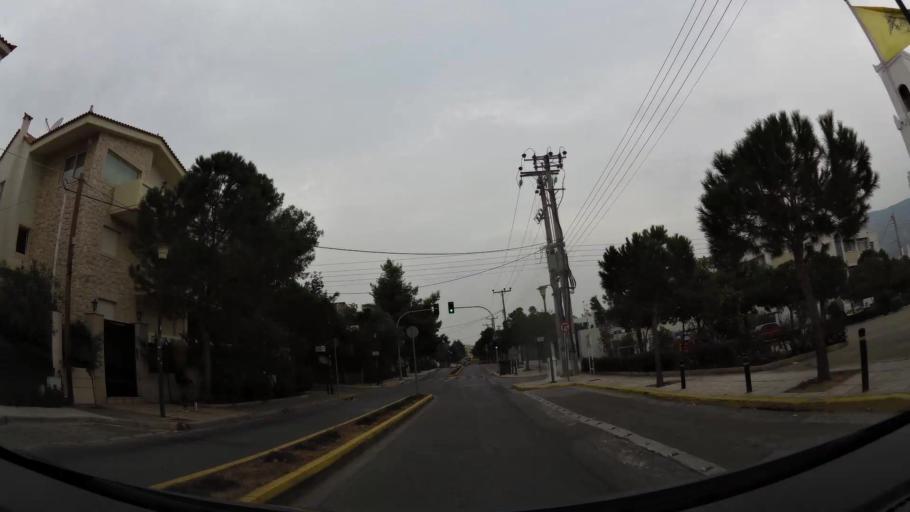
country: GR
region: Attica
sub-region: Nomarchia Athinas
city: Alimos
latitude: 37.9098
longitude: 23.7341
